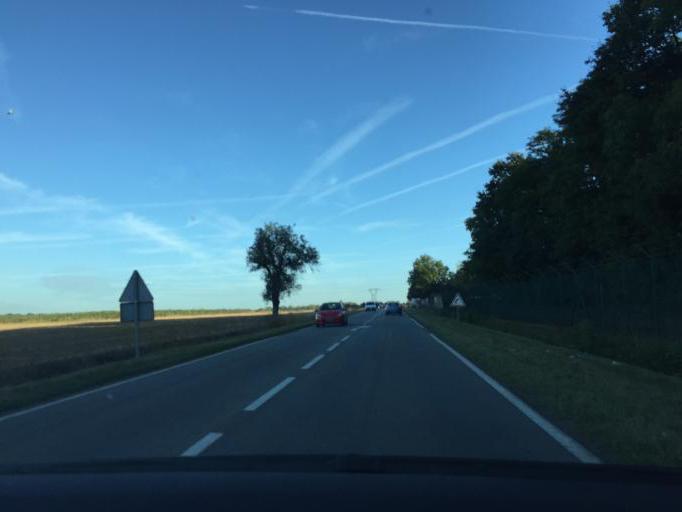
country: FR
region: Ile-de-France
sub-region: Departement des Yvelines
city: Jouy-en-Josas
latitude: 48.7467
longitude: 2.1653
